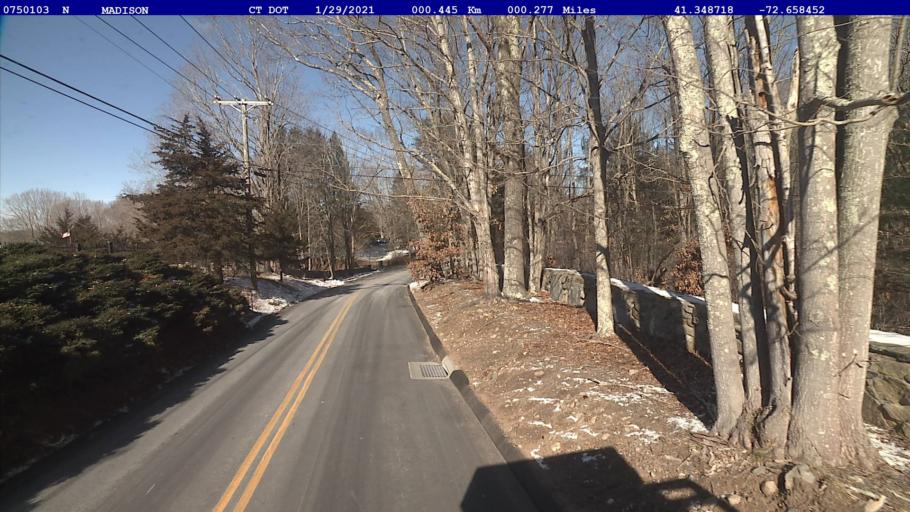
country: US
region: Connecticut
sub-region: New Haven County
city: Guilford
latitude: 41.3487
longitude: -72.6584
